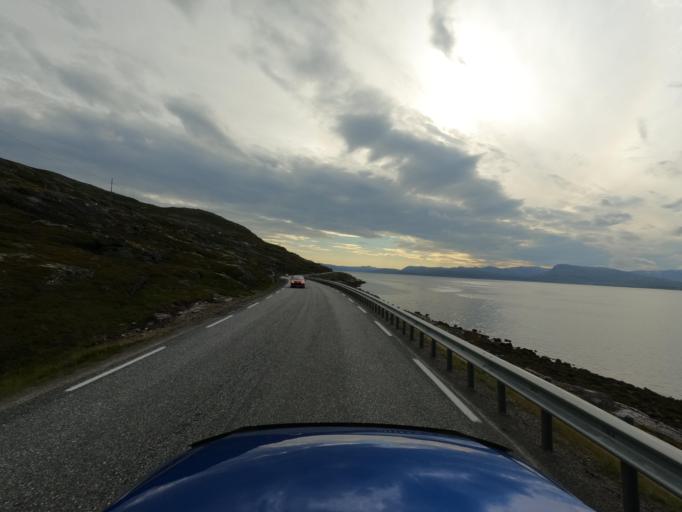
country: NO
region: Finnmark Fylke
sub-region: Hammerfest
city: Rypefjord
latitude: 70.5952
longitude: 23.6808
